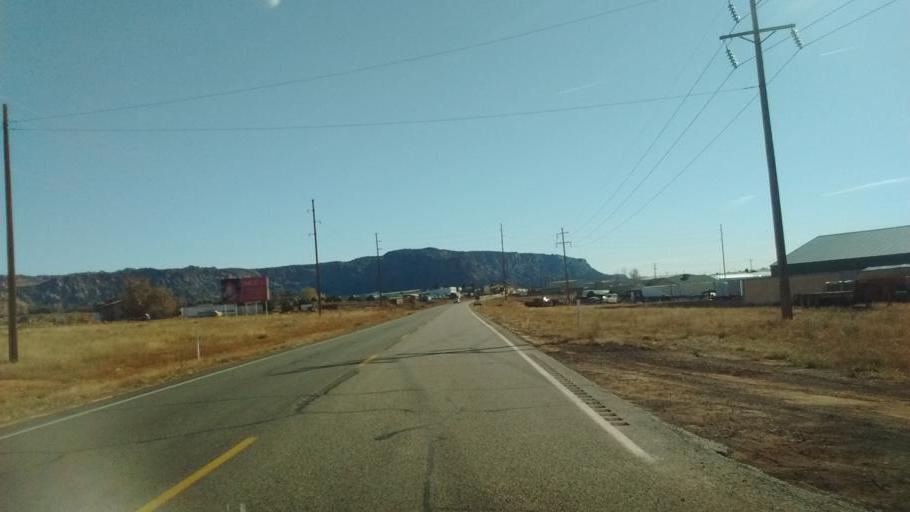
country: US
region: Arizona
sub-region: Mohave County
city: Colorado City
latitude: 37.0065
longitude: -113.0073
